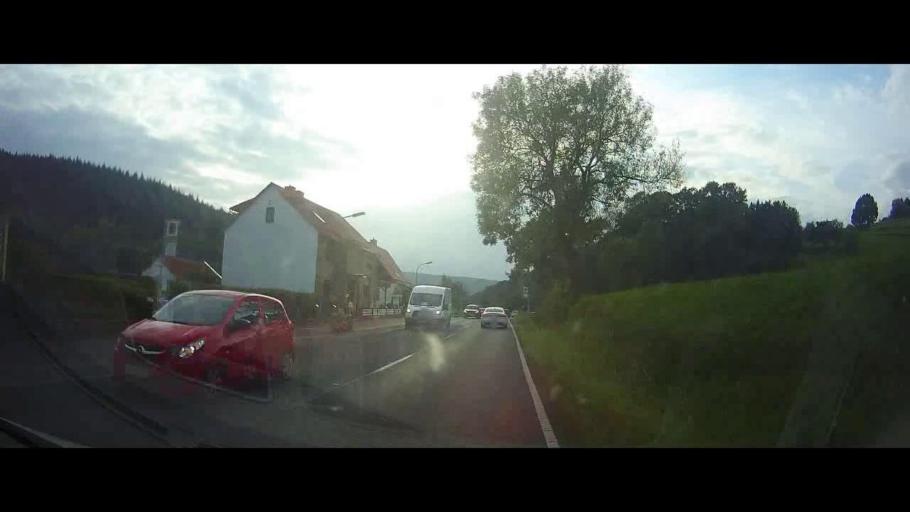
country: DE
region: Lower Saxony
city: Adelebsen
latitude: 51.5582
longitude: 9.7735
